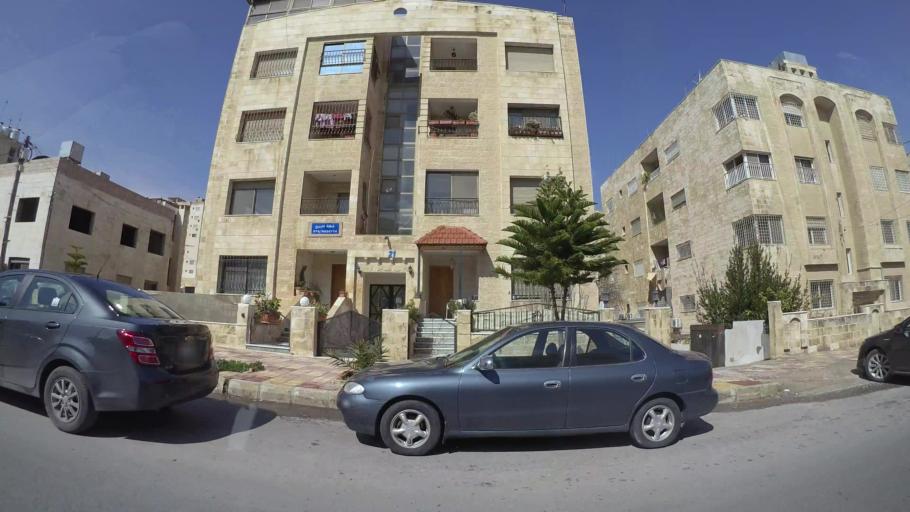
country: JO
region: Amman
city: Al Jubayhah
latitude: 31.9907
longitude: 35.9016
